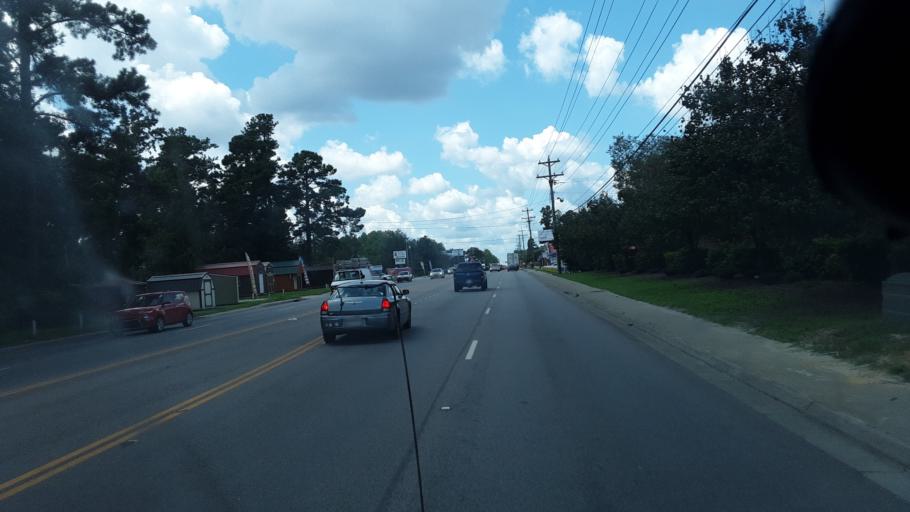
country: US
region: South Carolina
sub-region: Berkeley County
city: Sangaree
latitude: 33.0456
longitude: -80.1133
